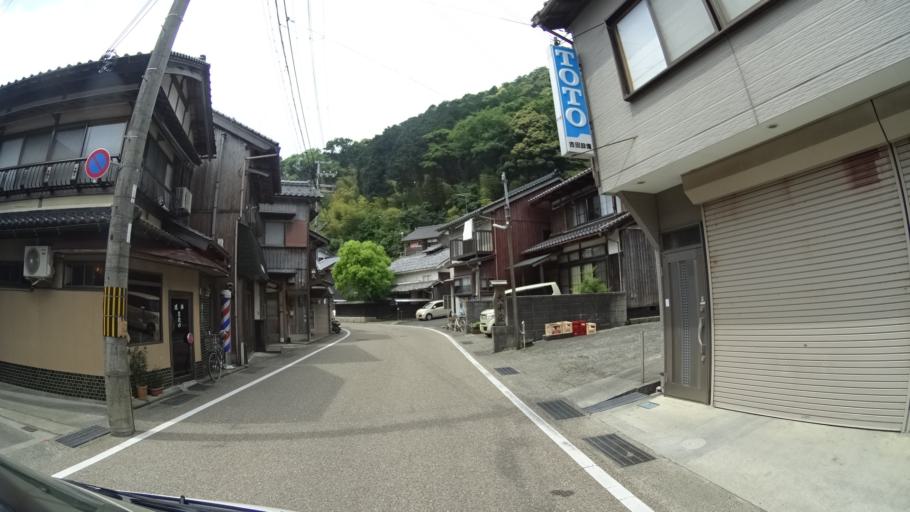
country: JP
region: Kyoto
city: Miyazu
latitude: 35.6750
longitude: 135.2866
